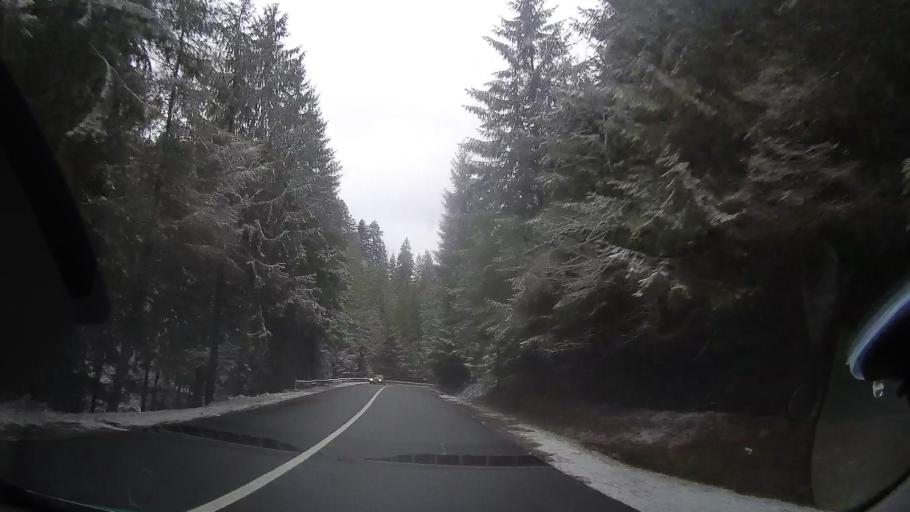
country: RO
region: Cluj
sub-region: Comuna Calatele
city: Calatele
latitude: 46.7362
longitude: 23.0390
